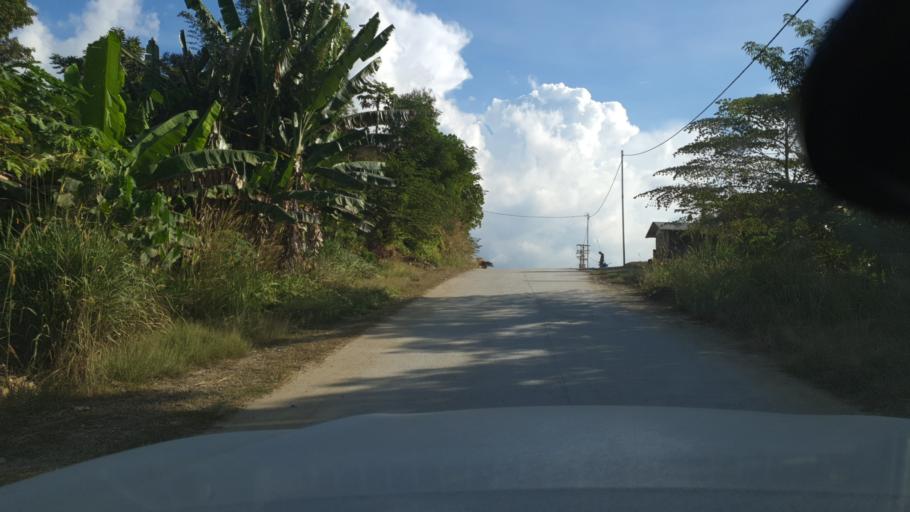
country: SB
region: Guadalcanal
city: Honiara
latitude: -9.4462
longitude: 159.9971
